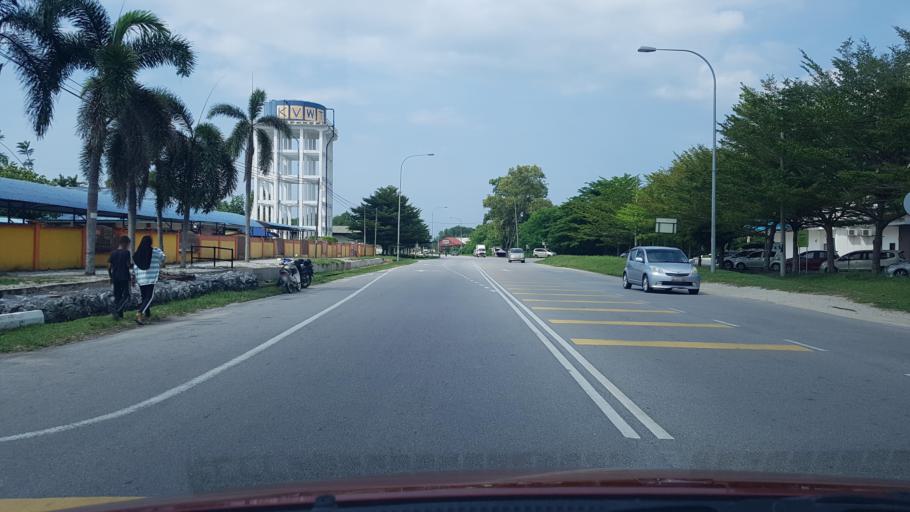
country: MY
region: Terengganu
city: Kuala Terengganu
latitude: 5.3581
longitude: 103.0953
